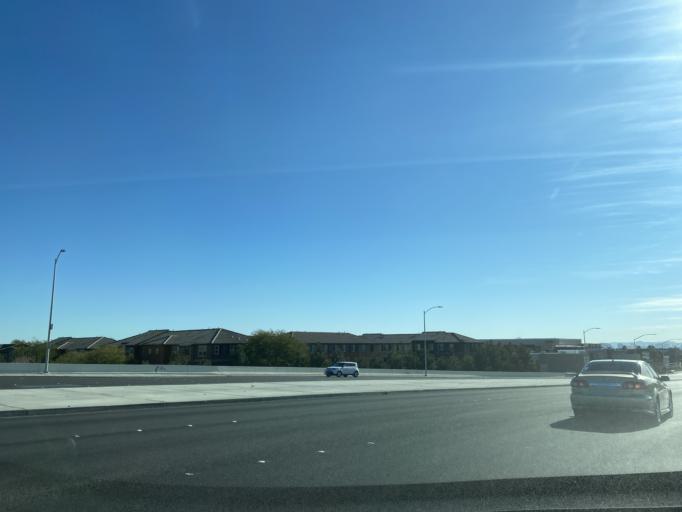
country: US
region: Nevada
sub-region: Clark County
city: North Las Vegas
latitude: 36.2740
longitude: -115.2068
